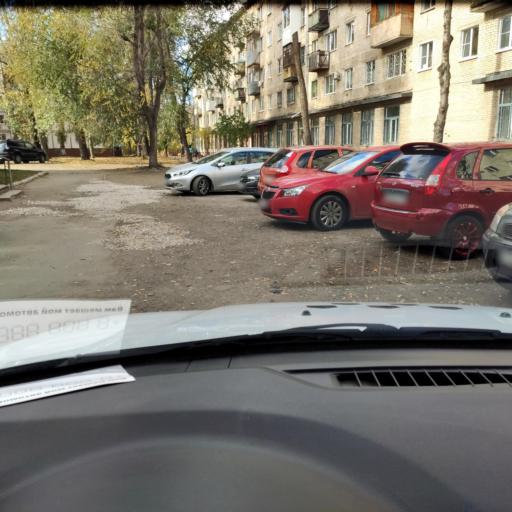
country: RU
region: Samara
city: Tol'yatti
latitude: 53.5128
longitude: 49.4282
